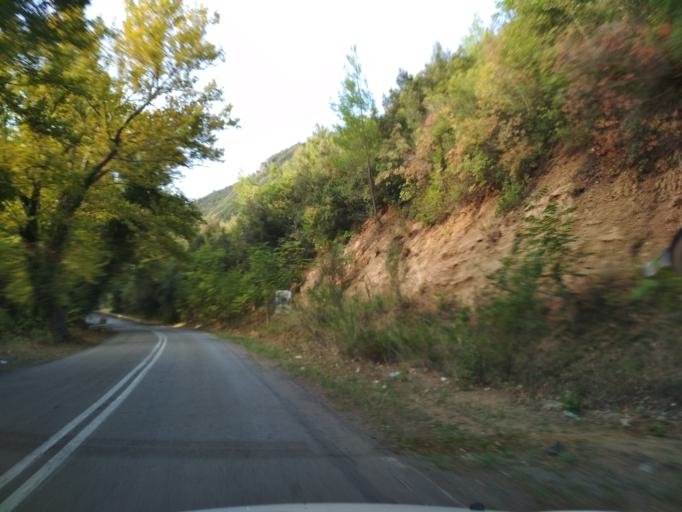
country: GR
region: Central Greece
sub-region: Nomos Evvoias
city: Mantoudi
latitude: 38.7782
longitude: 23.4701
